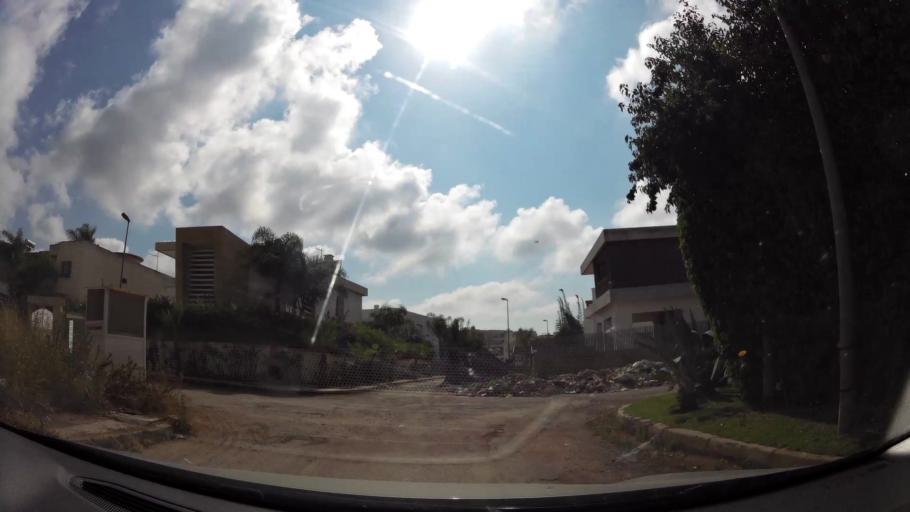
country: MA
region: Rabat-Sale-Zemmour-Zaer
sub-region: Skhirate-Temara
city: Temara
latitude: 33.9481
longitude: -6.8758
